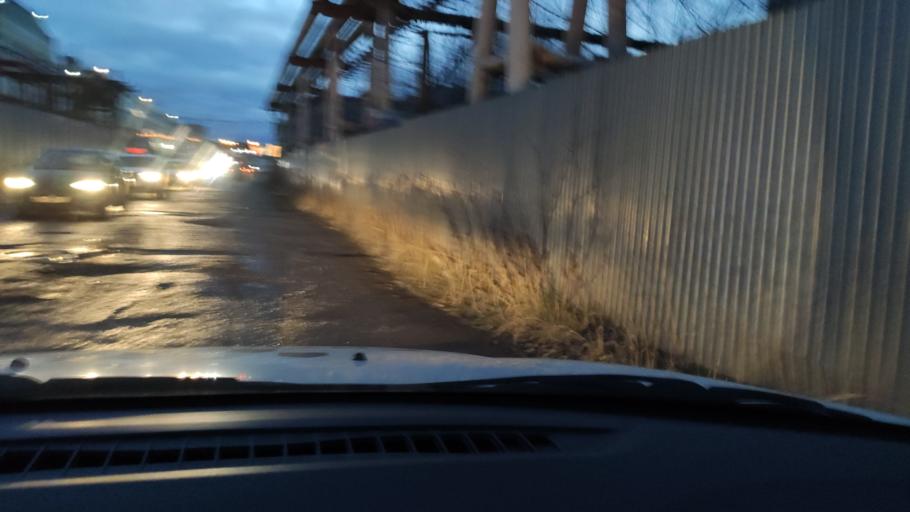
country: RU
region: Perm
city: Froly
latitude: 57.9623
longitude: 56.2721
